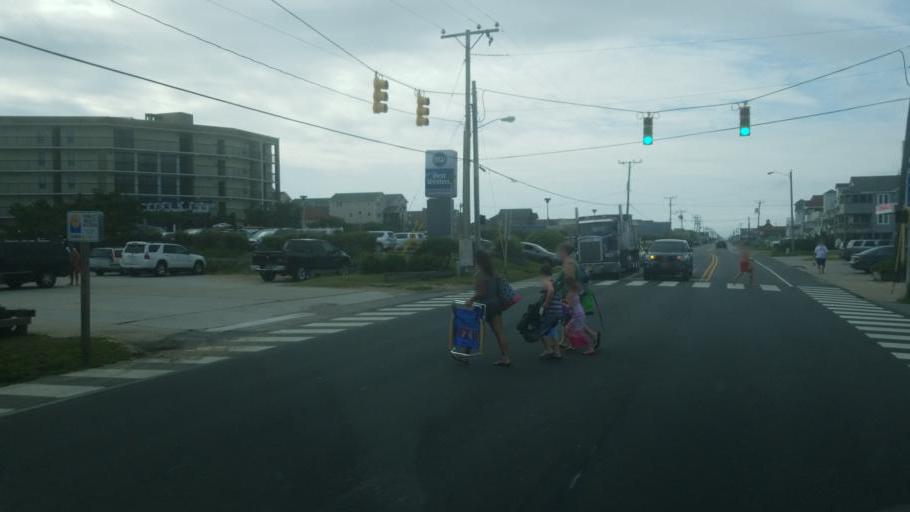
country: US
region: North Carolina
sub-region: Dare County
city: Kill Devil Hills
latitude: 36.0148
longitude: -75.6578
